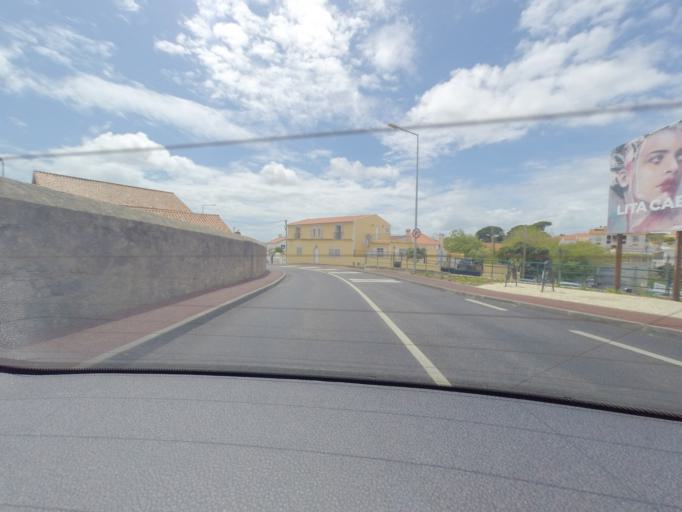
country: PT
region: Lisbon
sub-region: Cascais
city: Alcabideche
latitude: 38.7291
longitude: -9.3841
